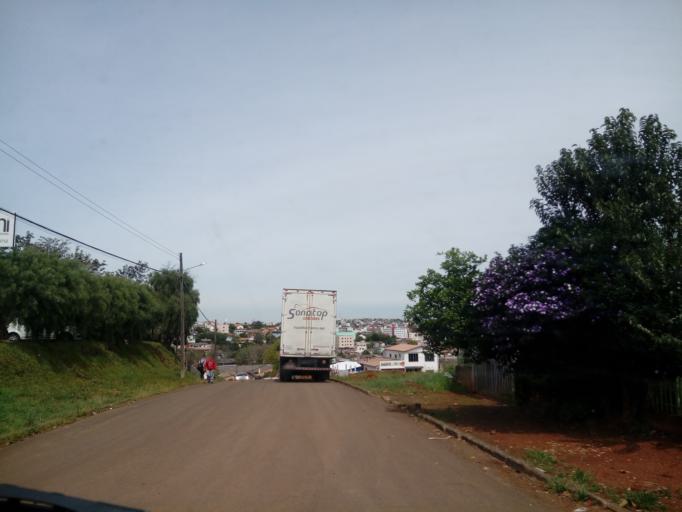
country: BR
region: Santa Catarina
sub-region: Chapeco
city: Chapeco
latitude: -27.0704
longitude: -52.6168
